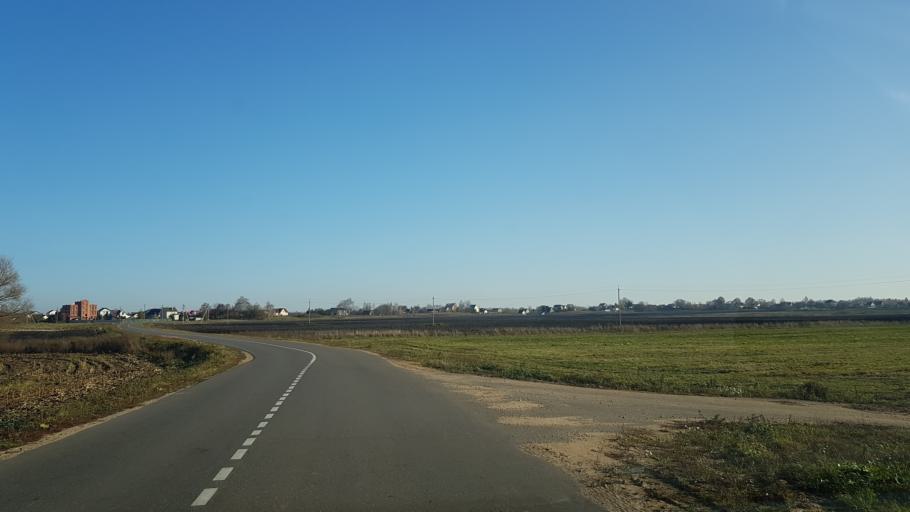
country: BY
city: Fanipol
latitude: 53.7206
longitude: 27.3053
